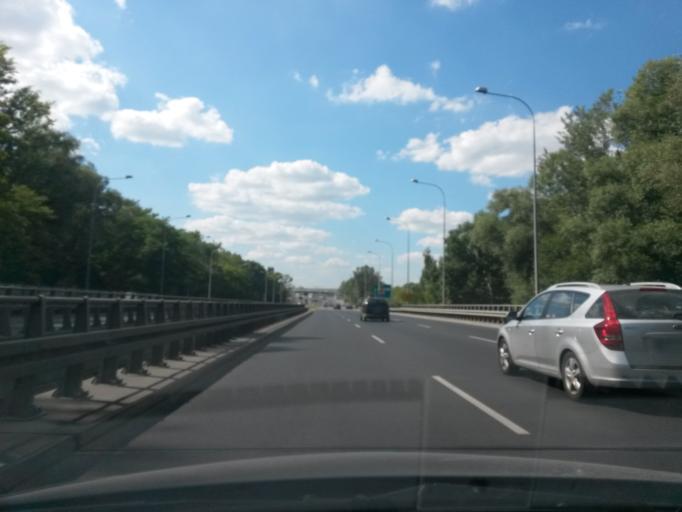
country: PL
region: Masovian Voivodeship
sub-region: Warszawa
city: Bielany
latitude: 52.3003
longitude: 20.9543
